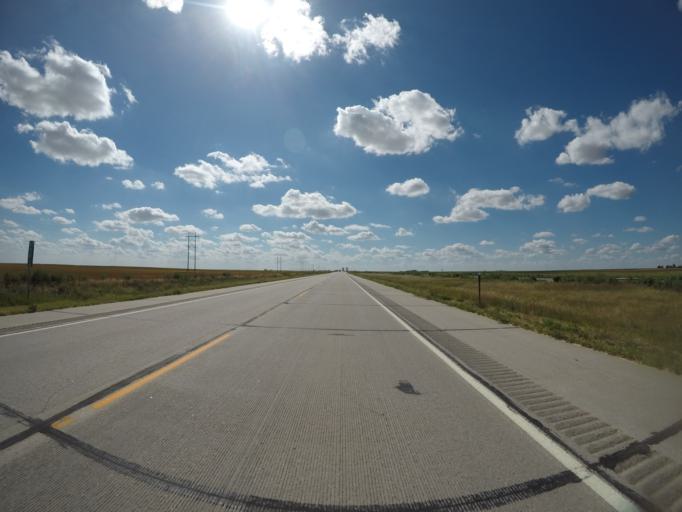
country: US
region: Colorado
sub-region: Phillips County
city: Holyoke
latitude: 40.6060
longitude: -102.4327
